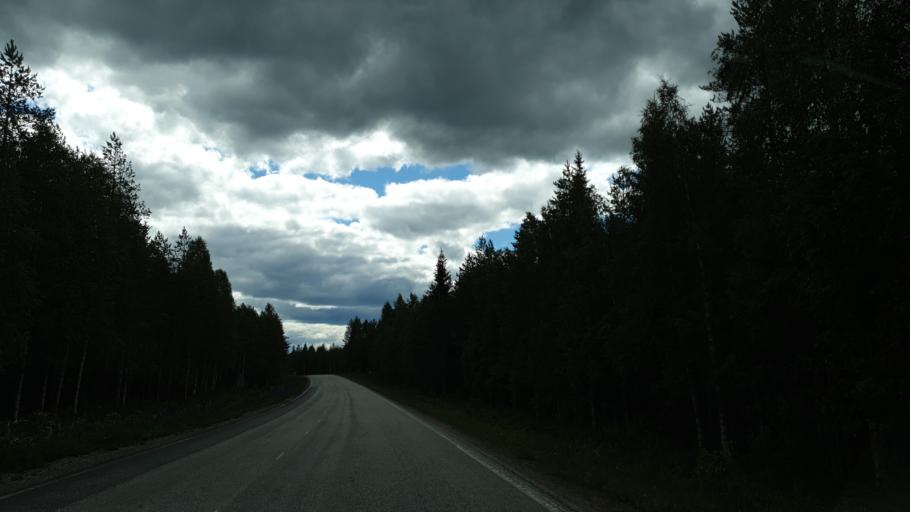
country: FI
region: Kainuu
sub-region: Kehys-Kainuu
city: Kuhmo
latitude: 63.9801
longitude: 29.6409
